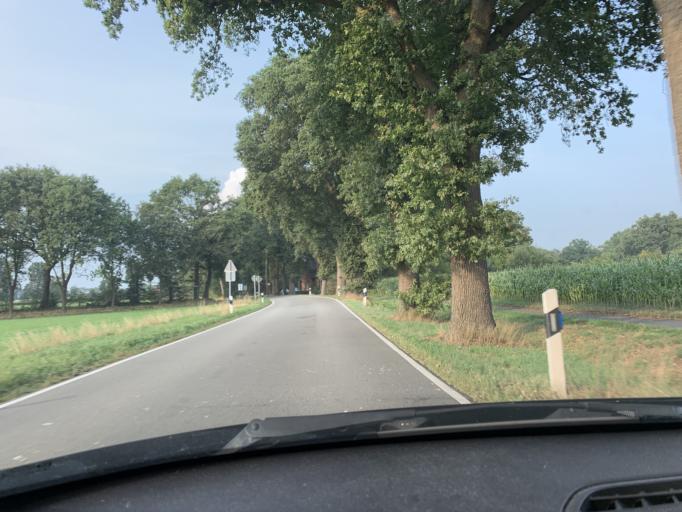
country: DE
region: Lower Saxony
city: Apen
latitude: 53.1807
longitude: 7.7807
